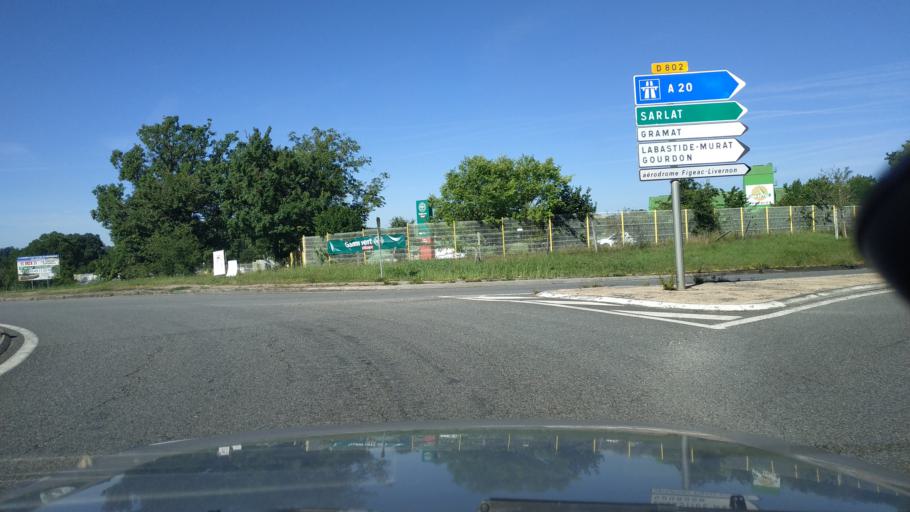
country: FR
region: Midi-Pyrenees
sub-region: Departement du Lot
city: Lacapelle-Marival
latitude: 44.6570
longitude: 1.8521
